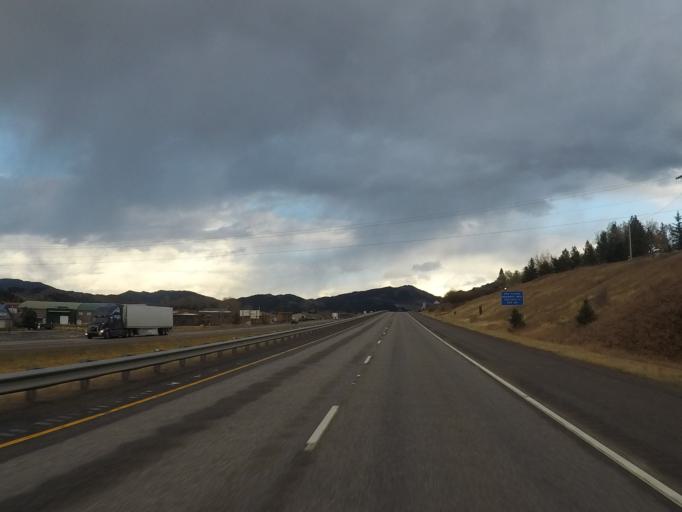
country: US
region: Montana
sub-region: Gallatin County
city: Bozeman
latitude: 45.6714
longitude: -111.0017
